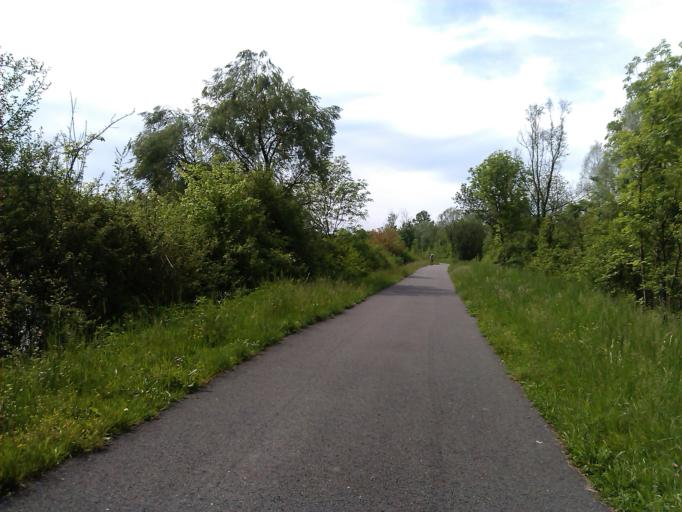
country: FR
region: Franche-Comte
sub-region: Departement du Doubs
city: Saint-Vit
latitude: 47.1666
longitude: 5.8237
